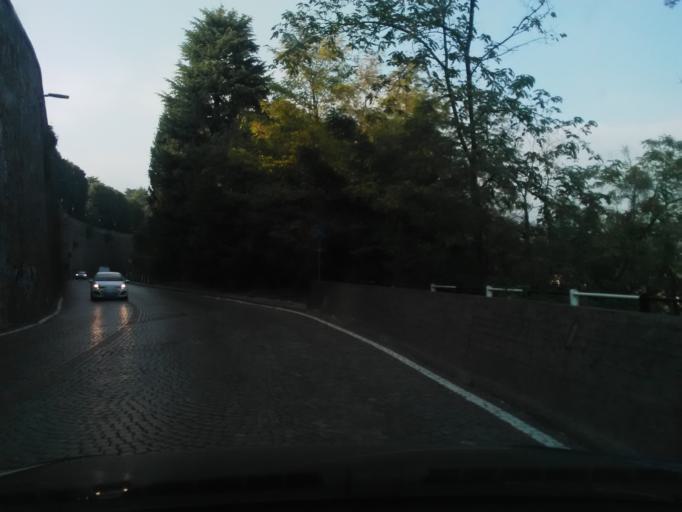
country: IT
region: Piedmont
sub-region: Provincia di Biella
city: Biella
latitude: 45.5663
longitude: 8.0616
